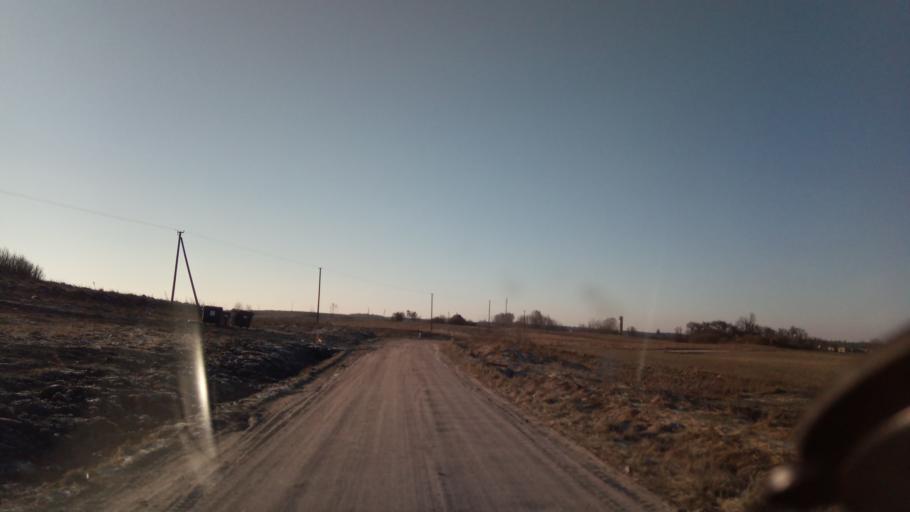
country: LT
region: Alytaus apskritis
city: Druskininkai
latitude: 54.0883
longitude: 23.9898
